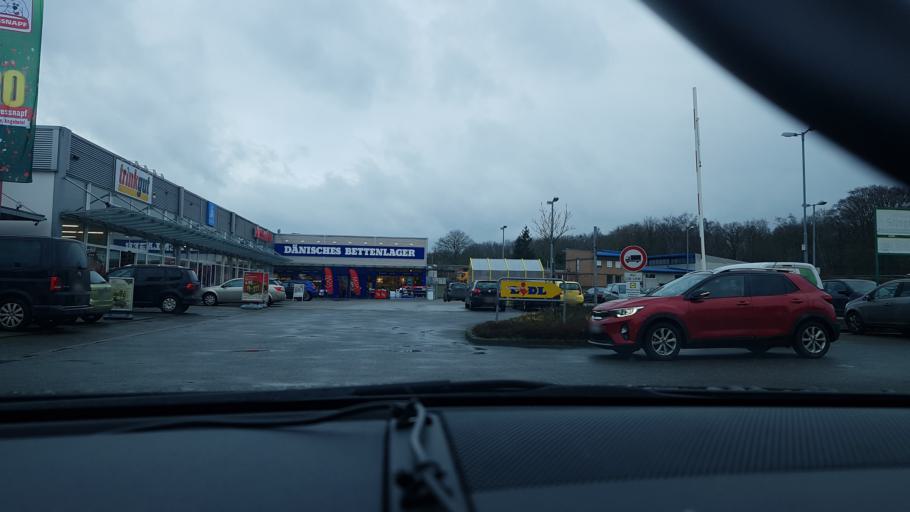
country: DE
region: North Rhine-Westphalia
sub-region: Regierungsbezirk Dusseldorf
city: Bruggen
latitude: 51.2453
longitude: 6.1945
